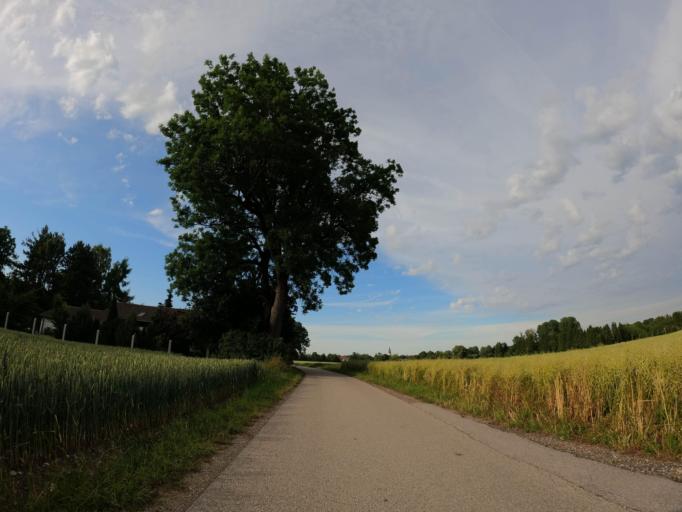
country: DE
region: Bavaria
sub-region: Upper Bavaria
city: Taufkirchen
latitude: 48.0388
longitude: 11.6095
